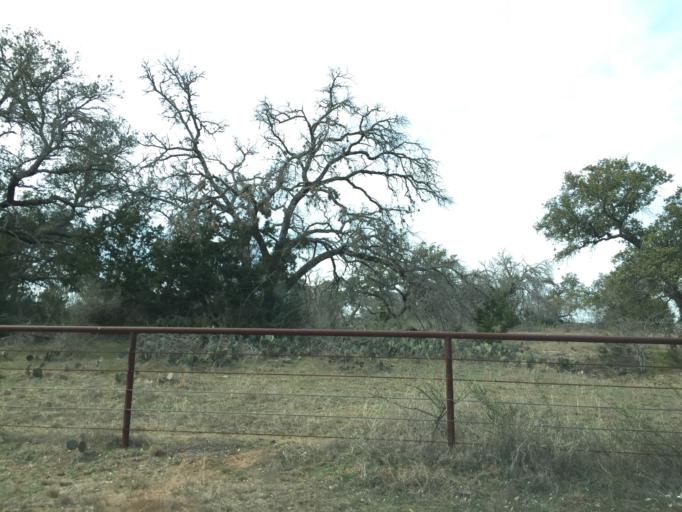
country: US
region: Texas
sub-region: Llano County
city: Kingsland
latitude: 30.4582
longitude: -98.6392
